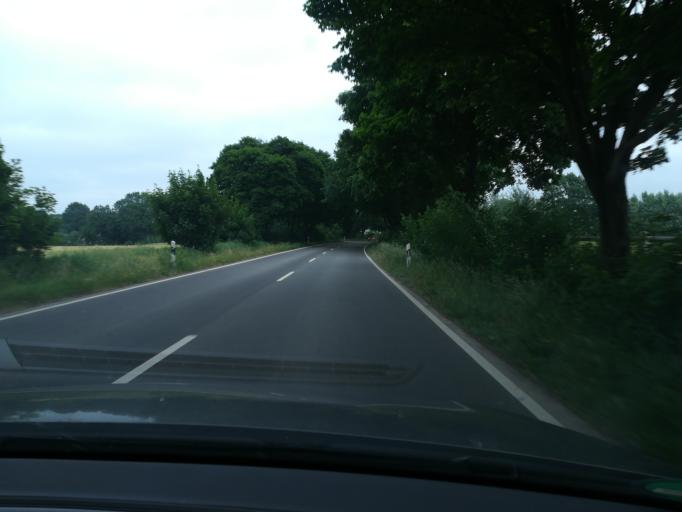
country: DE
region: Schleswig-Holstein
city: Siek
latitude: 53.6323
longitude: 10.3131
